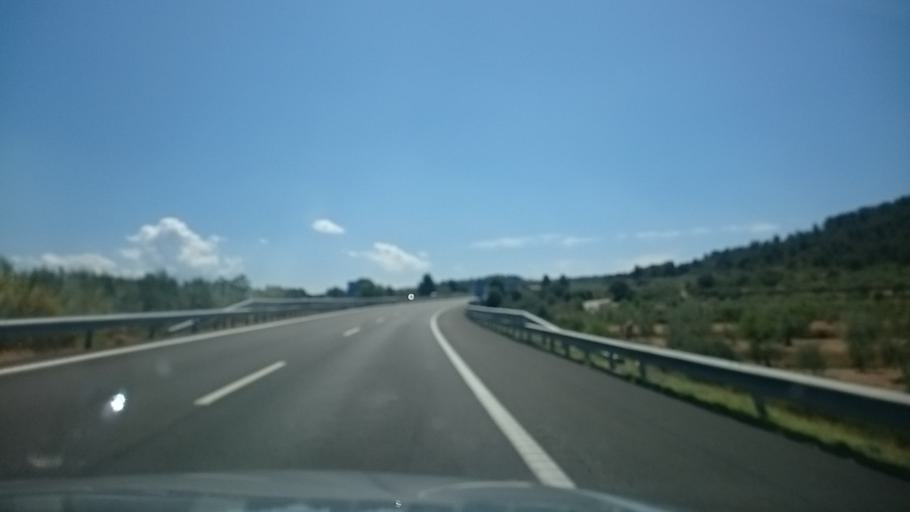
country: ES
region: Catalonia
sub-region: Provincia de Lleida
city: Vinaixa
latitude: 41.4408
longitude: 0.9205
